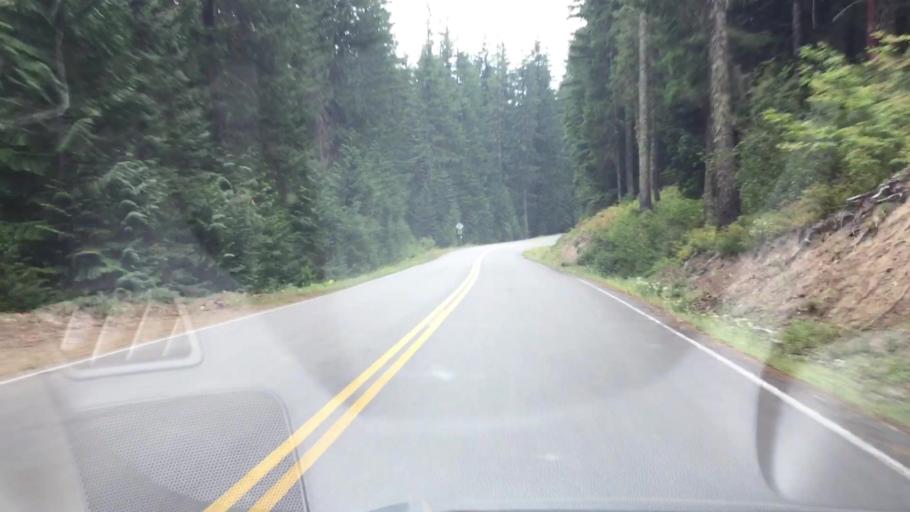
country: US
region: Washington
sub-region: Klickitat County
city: White Salmon
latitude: 46.1457
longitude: -121.6268
